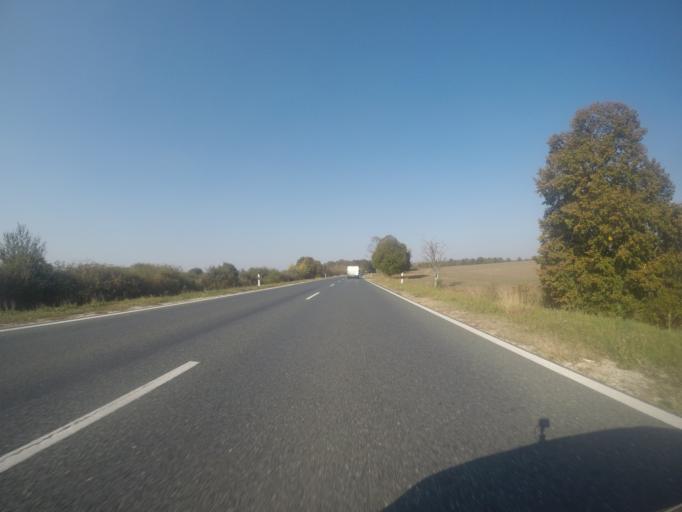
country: HU
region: Tolna
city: Bolcske
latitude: 46.7307
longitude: 18.8825
